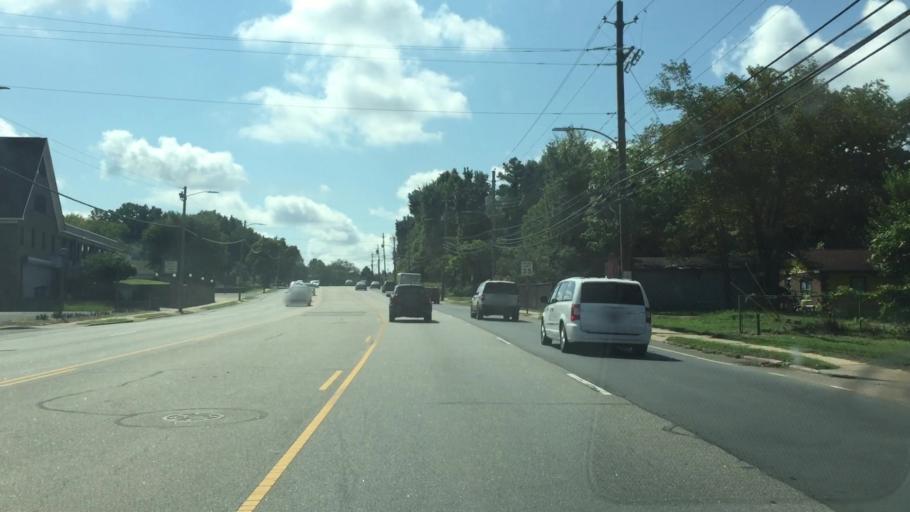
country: US
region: North Carolina
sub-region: Anson County
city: Wadesboro
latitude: 34.9732
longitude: -80.0829
